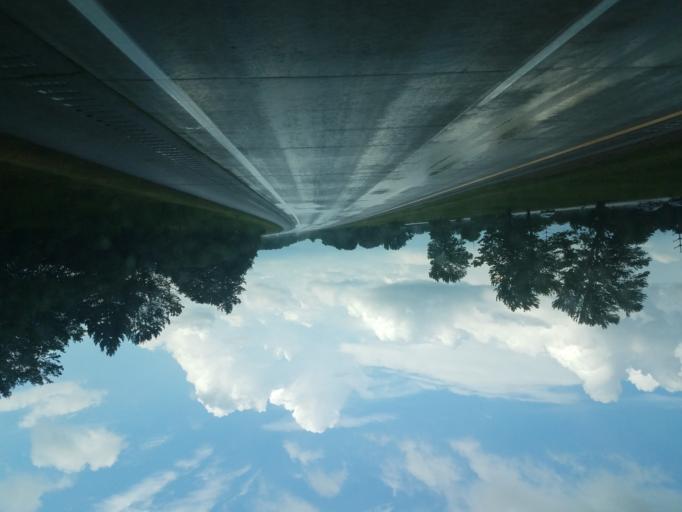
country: US
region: Michigan
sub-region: Calhoun County
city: Marshall
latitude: 42.2449
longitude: -84.9853
